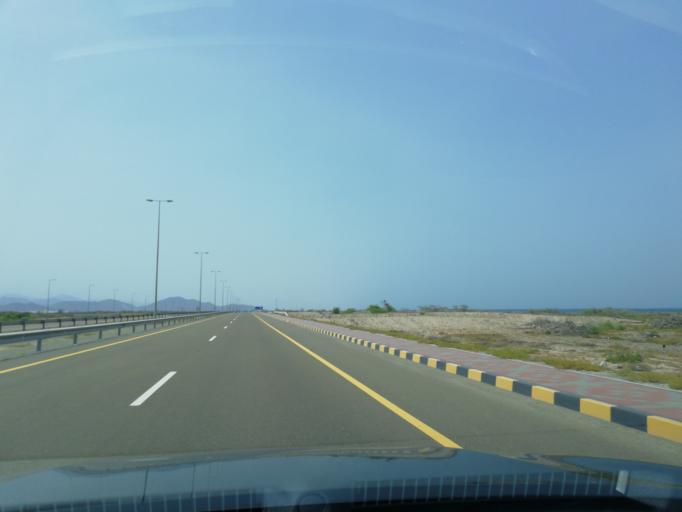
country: OM
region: Al Batinah
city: Shinas
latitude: 24.9109
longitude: 56.3917
